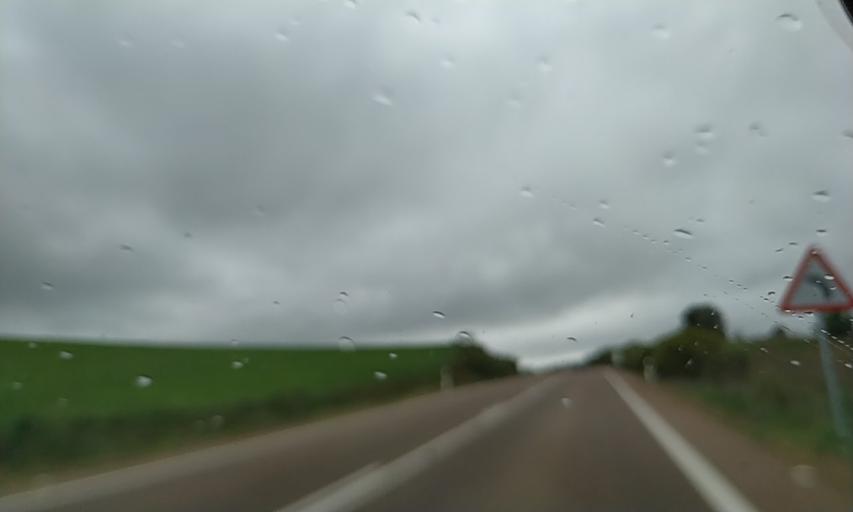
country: ES
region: Extremadura
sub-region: Provincia de Badajoz
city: Villar del Rey
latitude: 39.0578
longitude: -6.7855
